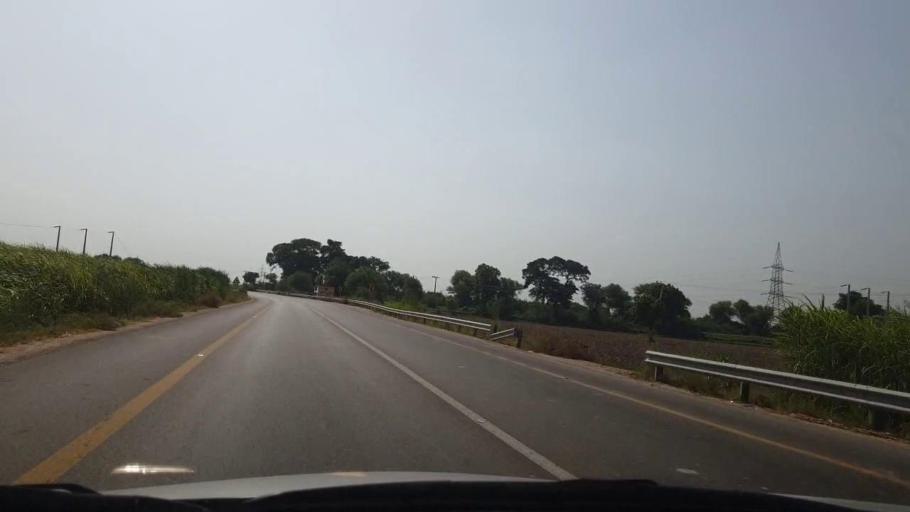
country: PK
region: Sindh
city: Matli
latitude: 25.0818
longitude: 68.6084
